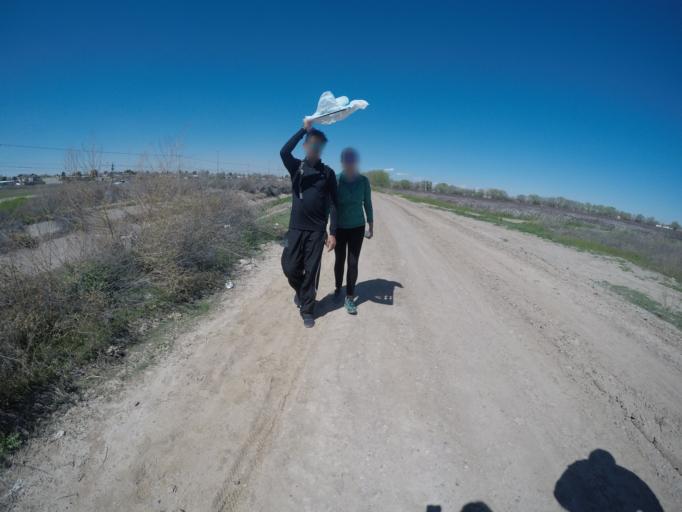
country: US
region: Texas
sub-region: El Paso County
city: Socorro Mission Number 1 Colonia
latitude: 31.6126
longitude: -106.3157
